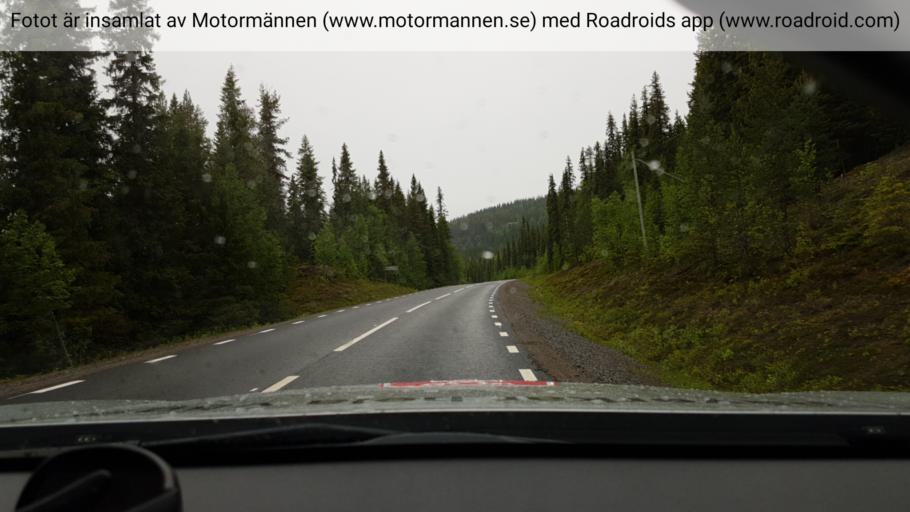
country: SE
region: Vaesterbotten
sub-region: Storumans Kommun
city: Fristad
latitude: 65.8093
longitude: 16.8826
